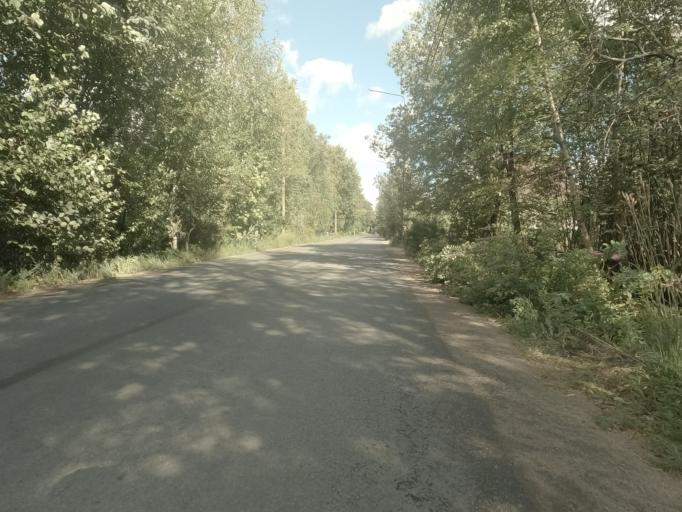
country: RU
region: Leningrad
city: Vsevolozhsk
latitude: 60.0081
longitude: 30.6560
